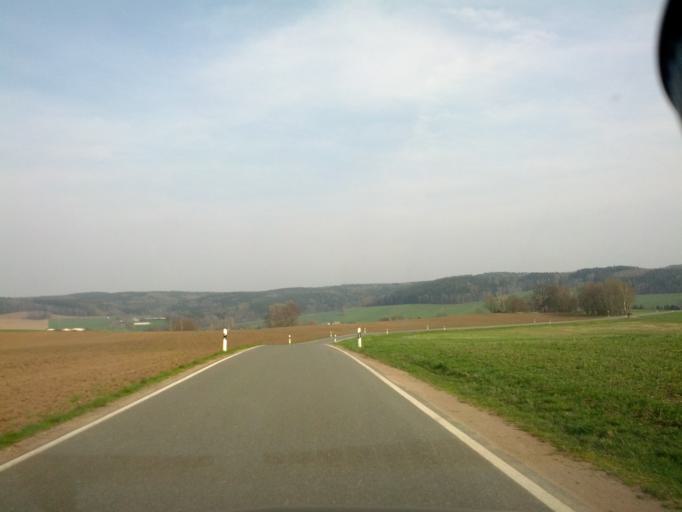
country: DE
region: Saxony
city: Stutzengrun
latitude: 50.5758
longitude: 12.5230
